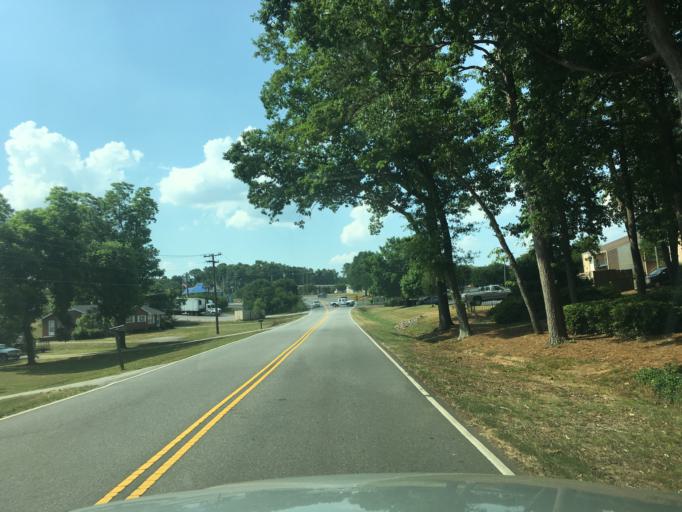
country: US
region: South Carolina
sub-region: Anderson County
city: Anderson
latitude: 34.5328
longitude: -82.6305
